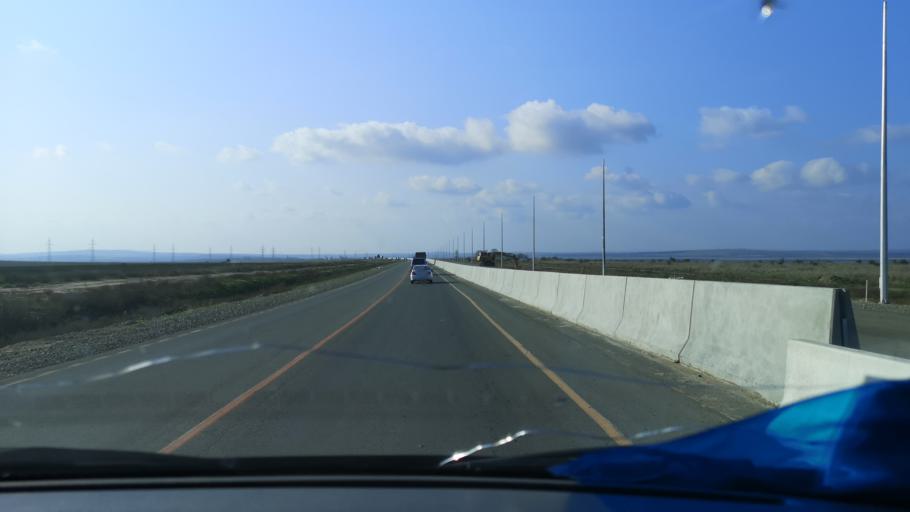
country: RU
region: Krasnodarskiy
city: Starotitarovskaya
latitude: 45.2340
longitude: 37.1075
